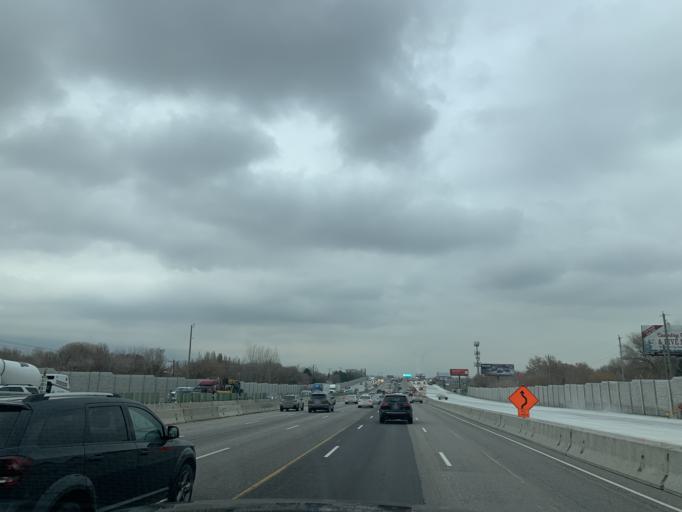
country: US
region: Utah
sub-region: Utah County
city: Lehi
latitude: 40.4026
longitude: -111.8525
